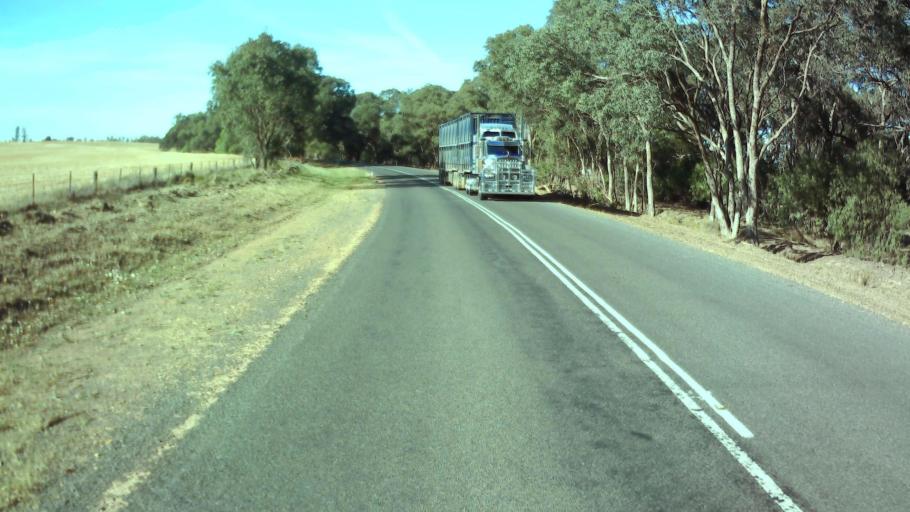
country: AU
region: New South Wales
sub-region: Weddin
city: Grenfell
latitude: -33.9938
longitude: 148.1333
